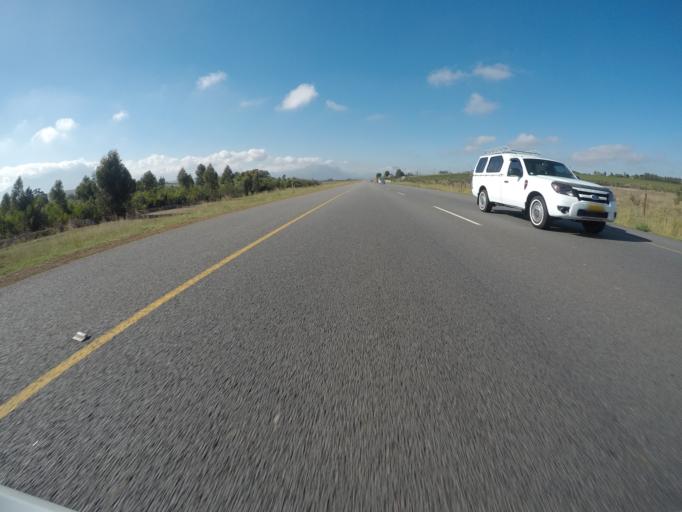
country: ZA
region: Western Cape
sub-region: City of Cape Town
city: Kraaifontein
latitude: -33.8560
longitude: 18.8083
